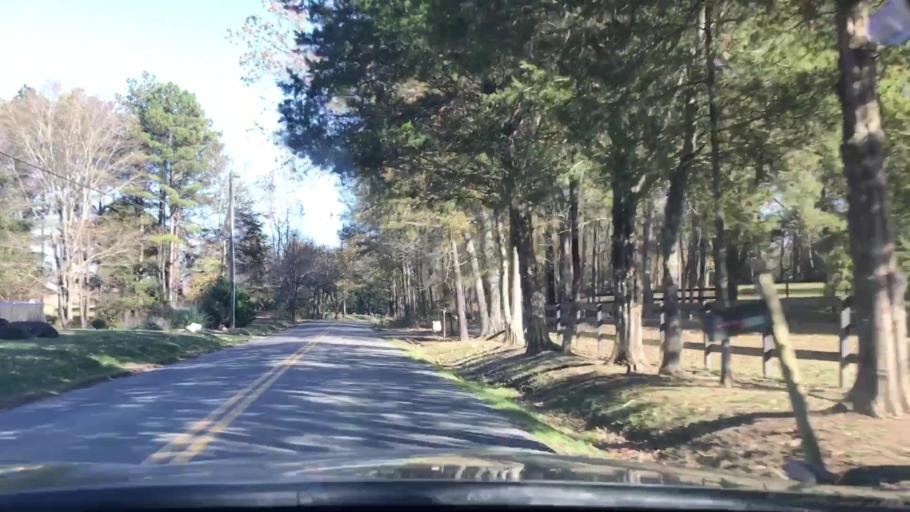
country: US
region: Virginia
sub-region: Henrico County
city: Short Pump
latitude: 37.6671
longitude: -77.7055
